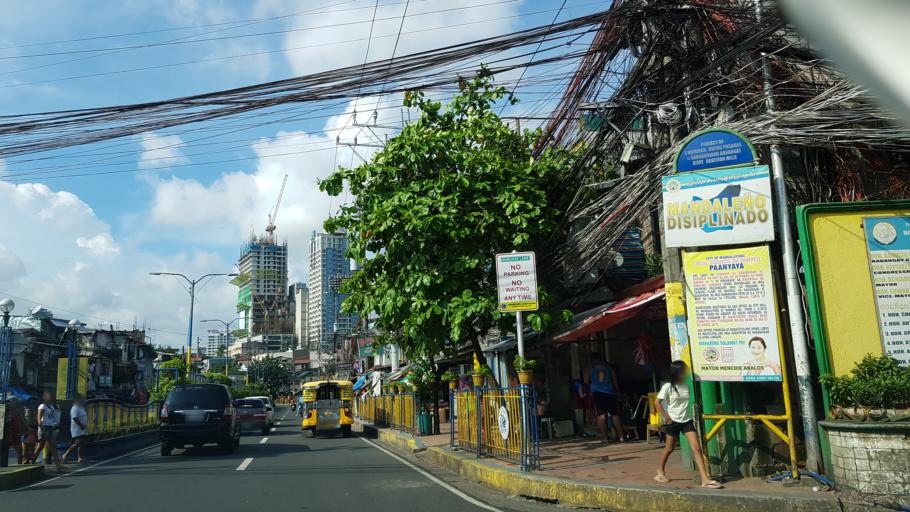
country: PH
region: Metro Manila
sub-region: Mandaluyong
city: Mandaluyong City
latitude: 14.5859
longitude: 121.0377
